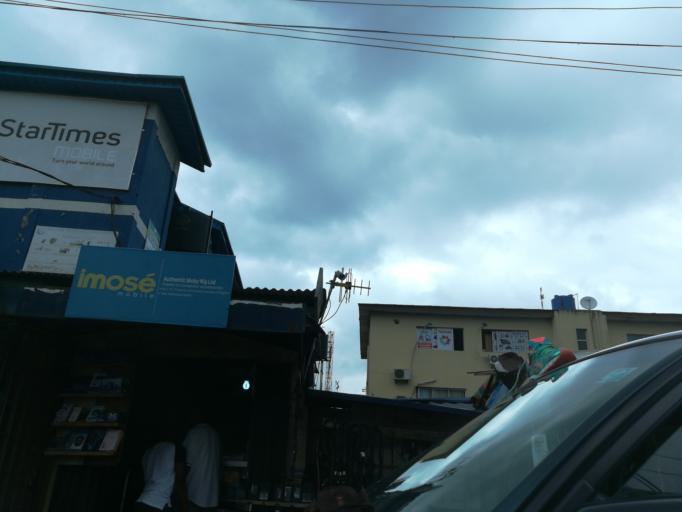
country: NG
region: Lagos
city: Ikeja
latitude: 6.5941
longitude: 3.3406
